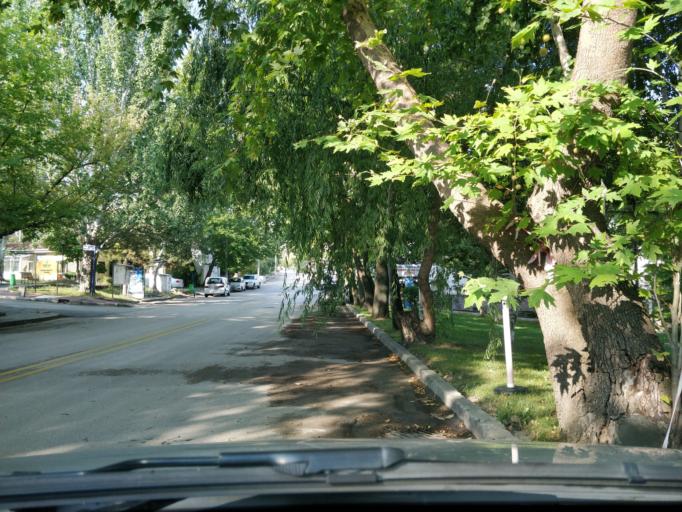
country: TR
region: Ankara
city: Batikent
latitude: 39.8937
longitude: 32.7188
